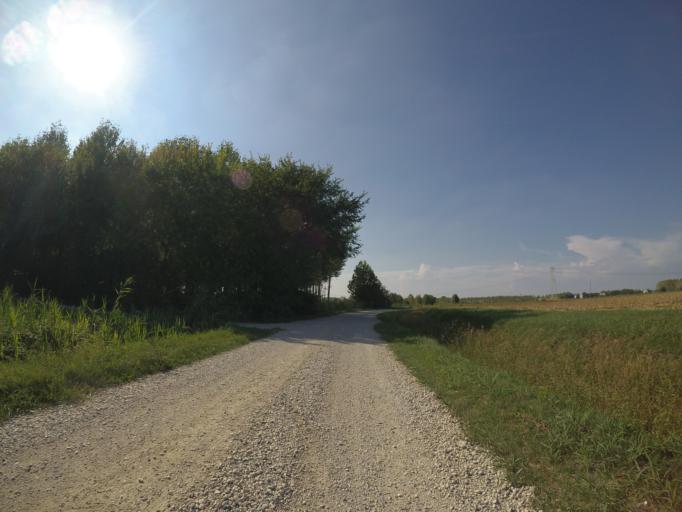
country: IT
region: Friuli Venezia Giulia
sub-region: Provincia di Udine
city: Pocenia
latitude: 45.8246
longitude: 13.1119
